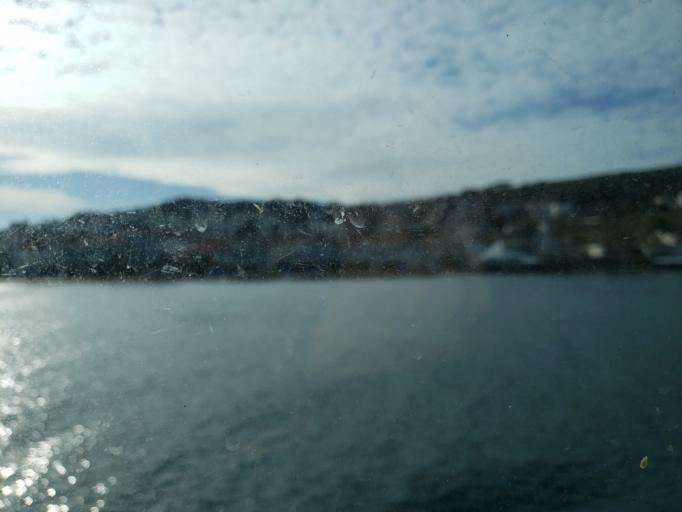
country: TR
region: Istanbul
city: Kinali
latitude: 40.9088
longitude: 29.0580
